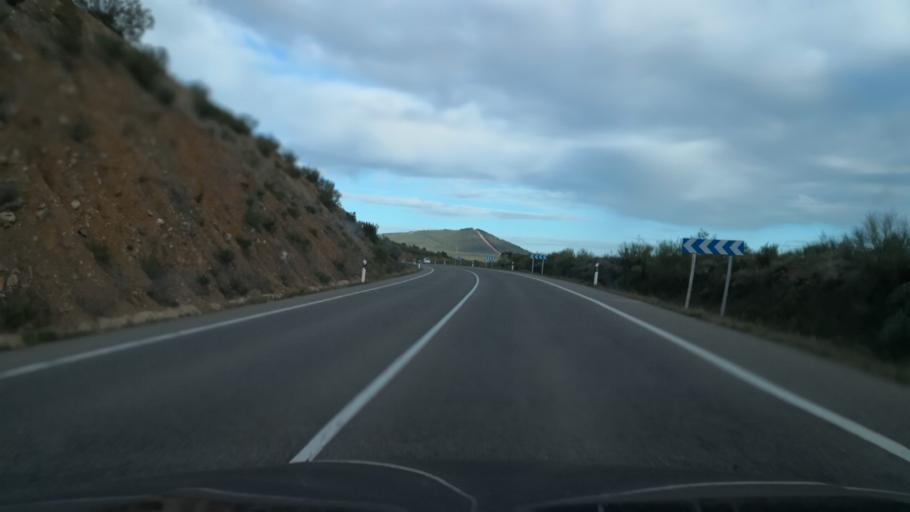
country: ES
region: Extremadura
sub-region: Provincia de Caceres
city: Pedroso de Acim
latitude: 39.8453
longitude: -6.4090
